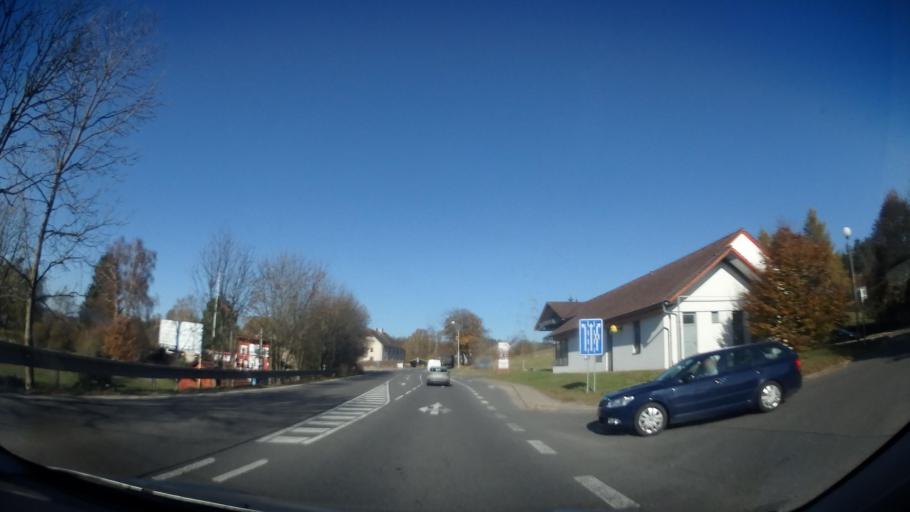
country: CZ
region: Pardubicky
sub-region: Okres Chrudim
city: Nasavrky
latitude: 49.7897
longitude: 15.8130
